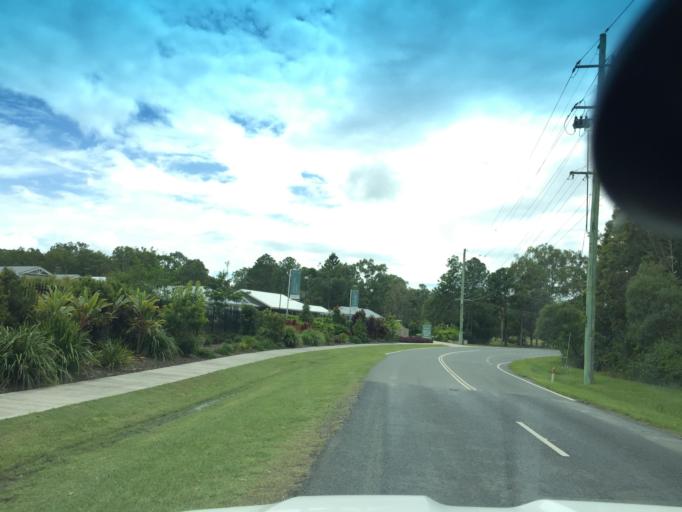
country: AU
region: Queensland
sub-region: Moreton Bay
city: Burpengary
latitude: -27.1693
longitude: 152.9870
